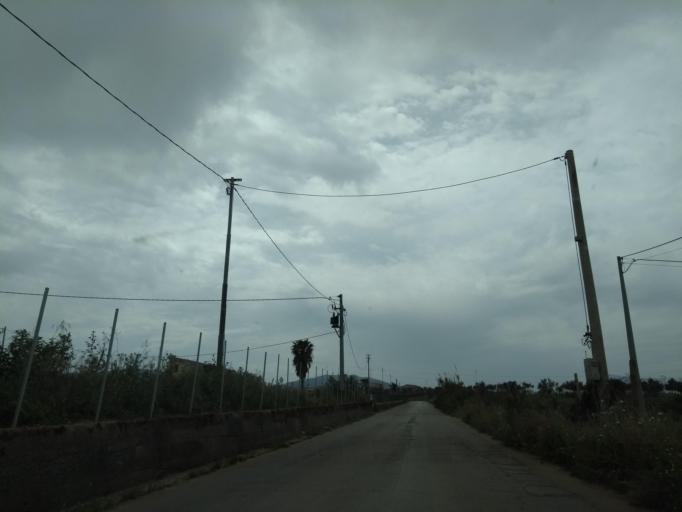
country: IT
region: Sicily
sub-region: Palermo
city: Partinico
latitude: 38.0007
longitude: 13.0671
